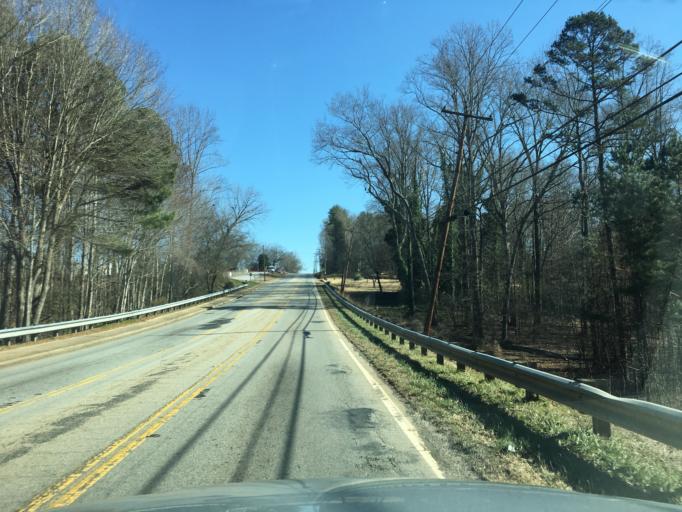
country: US
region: South Carolina
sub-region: Pickens County
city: Liberty
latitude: 34.7861
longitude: -82.7045
